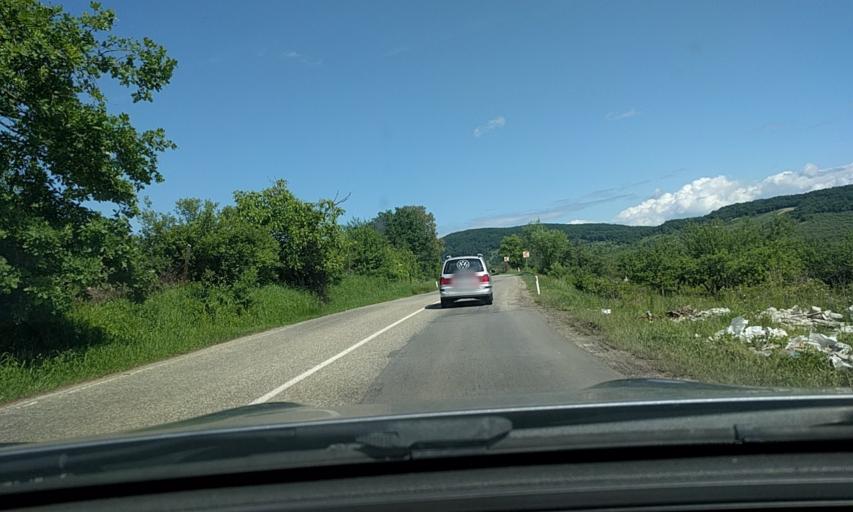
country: RO
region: Bistrita-Nasaud
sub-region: Municipiul Bistrita
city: Unirea
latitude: 47.1681
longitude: 24.4995
